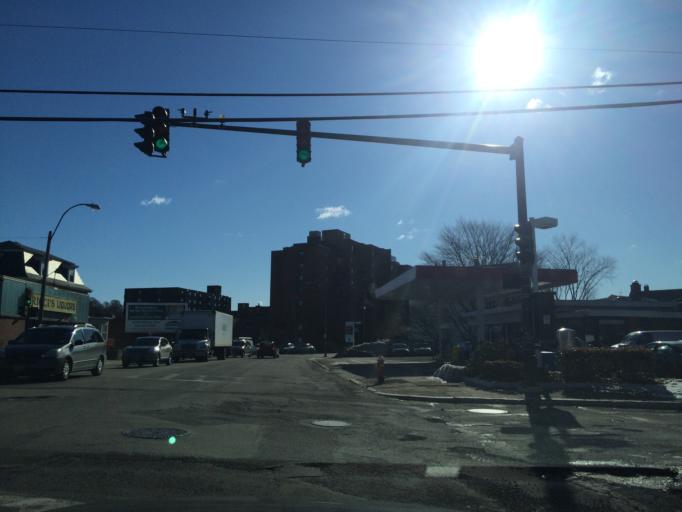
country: US
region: Massachusetts
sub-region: Middlesex County
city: Watertown
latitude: 42.3699
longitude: -71.1917
